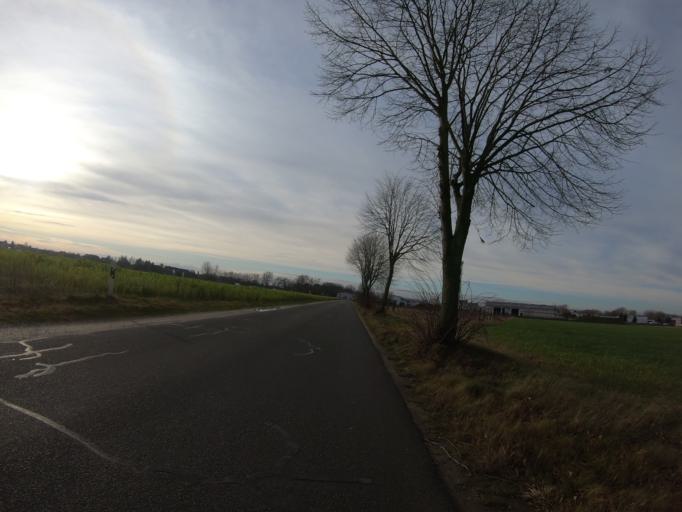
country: DE
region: Lower Saxony
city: Meinersen
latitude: 52.4817
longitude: 10.3669
